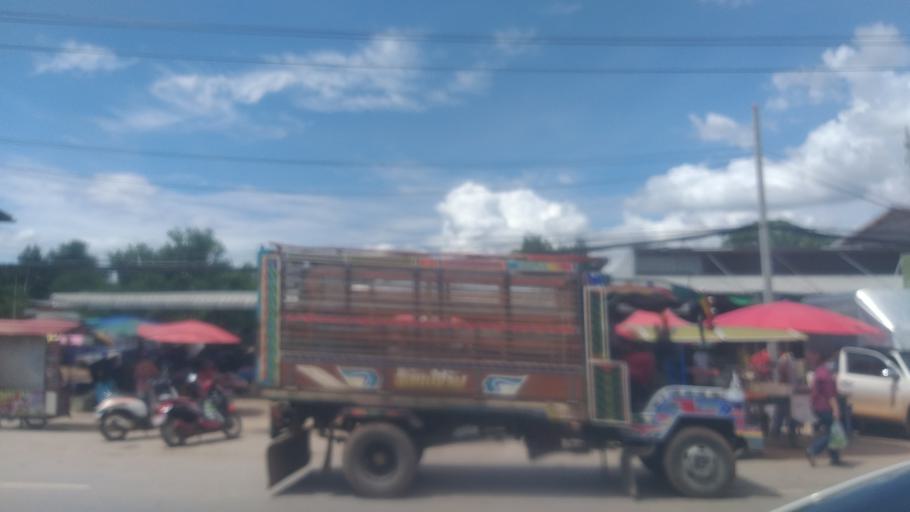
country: TH
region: Nakhon Ratchasima
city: Phra Thong Kham
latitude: 15.2670
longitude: 102.0206
